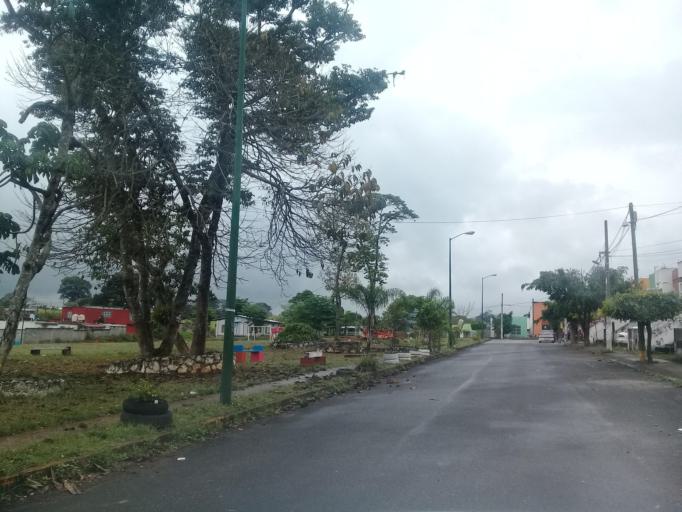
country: MX
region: Veracruz
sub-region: Cordoba
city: San Jose de Tapia
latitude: 18.8388
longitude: -96.9543
